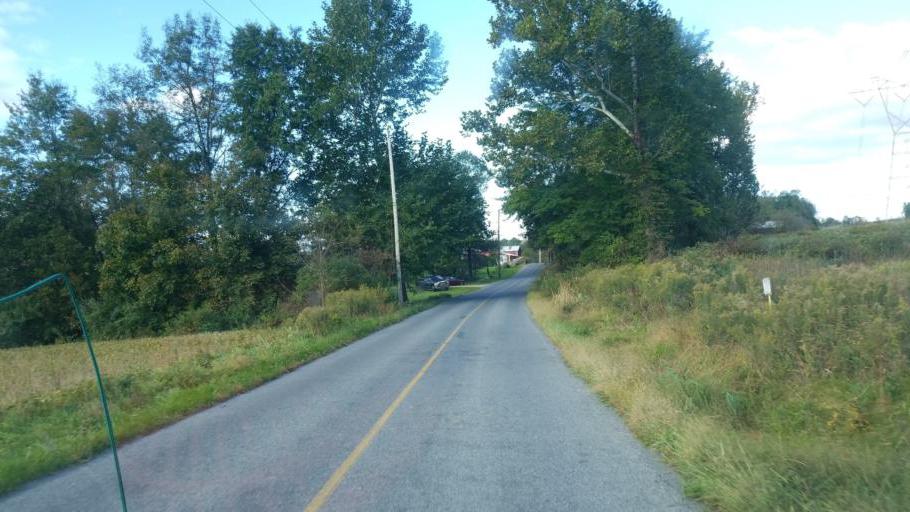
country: US
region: Pennsylvania
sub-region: Adams County
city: Biglerville
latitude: 39.8833
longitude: -77.3211
